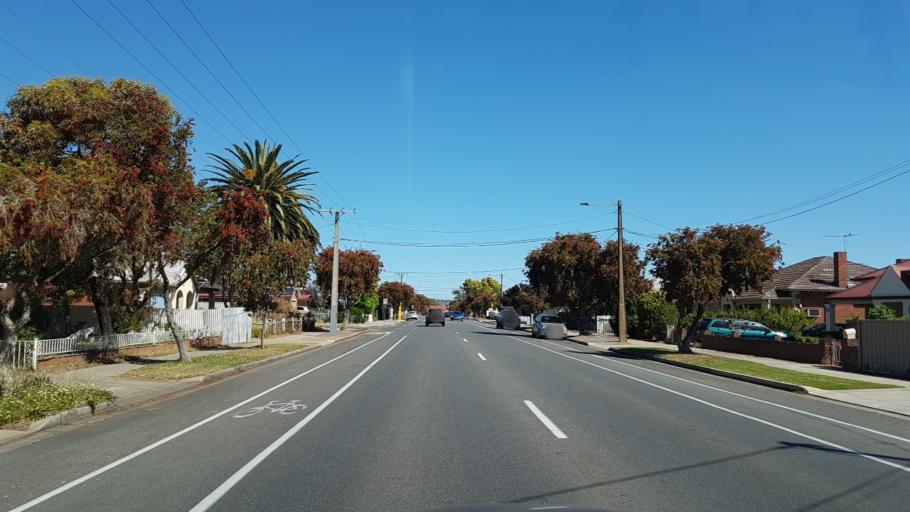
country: AU
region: South Australia
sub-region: Marion
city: South Plympton
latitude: -34.9642
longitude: 138.5636
